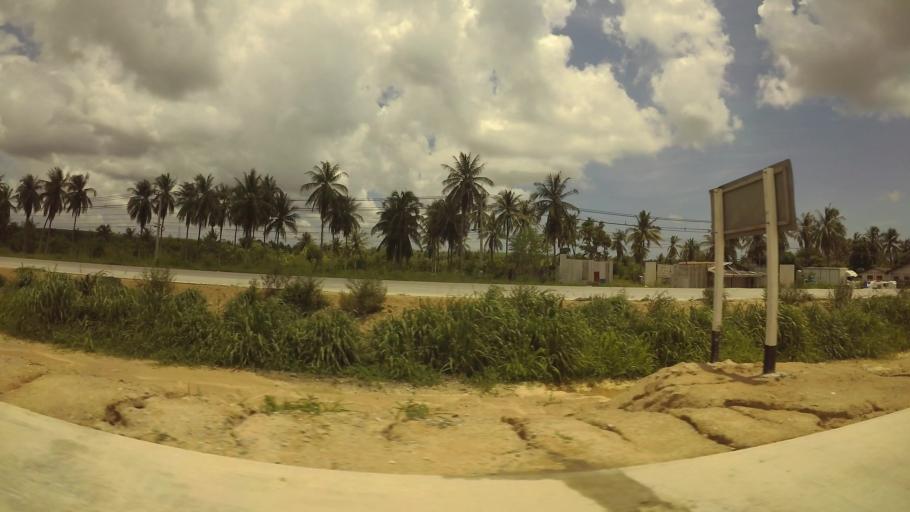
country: TH
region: Rayong
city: Ban Chang
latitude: 12.8916
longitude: 101.0462
